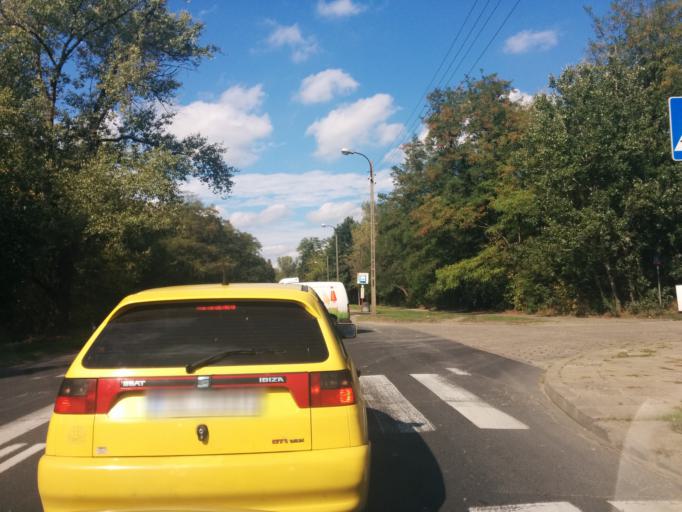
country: PL
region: Masovian Voivodeship
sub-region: Warszawa
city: Targowek
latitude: 52.3011
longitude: 21.0113
